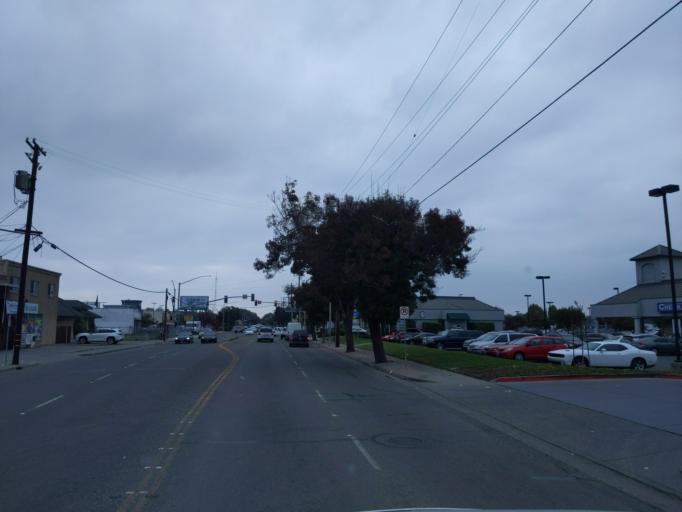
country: US
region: California
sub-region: San Joaquin County
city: August
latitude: 37.9614
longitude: -121.2689
